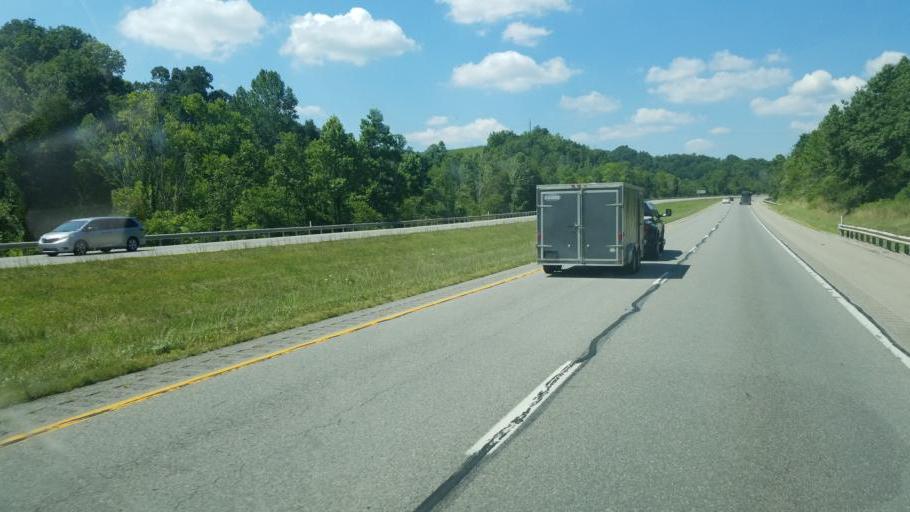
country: US
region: West Virginia
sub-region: Kanawha County
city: Sissonville
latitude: 38.5302
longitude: -81.6447
